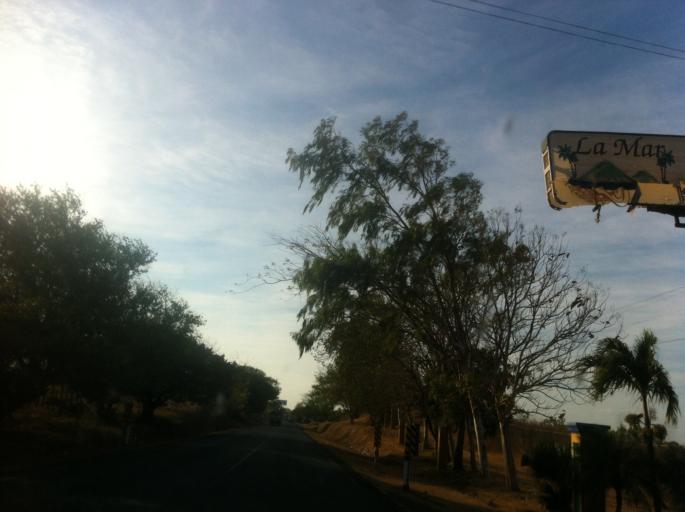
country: NI
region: Rivas
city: Rivas
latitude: 11.3505
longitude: -85.7383
